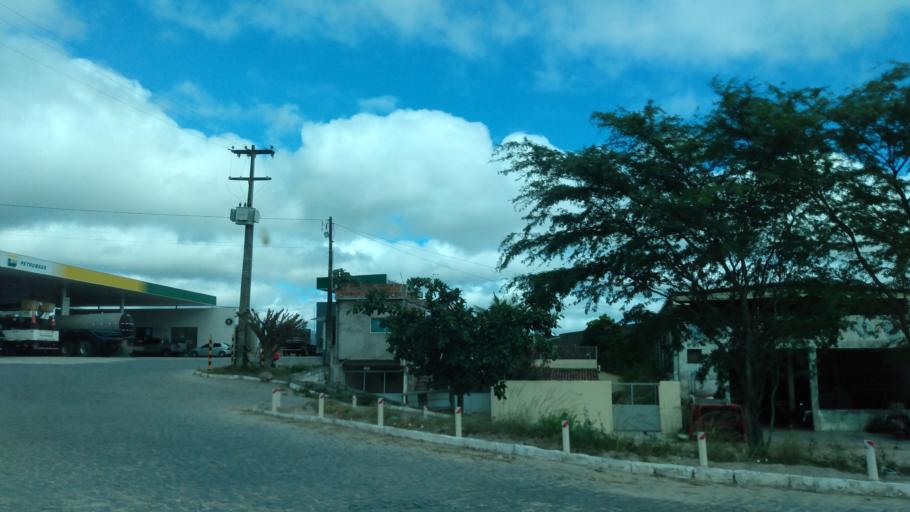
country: BR
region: Pernambuco
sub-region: Caruaru
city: Caruaru
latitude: -8.3097
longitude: -35.9903
